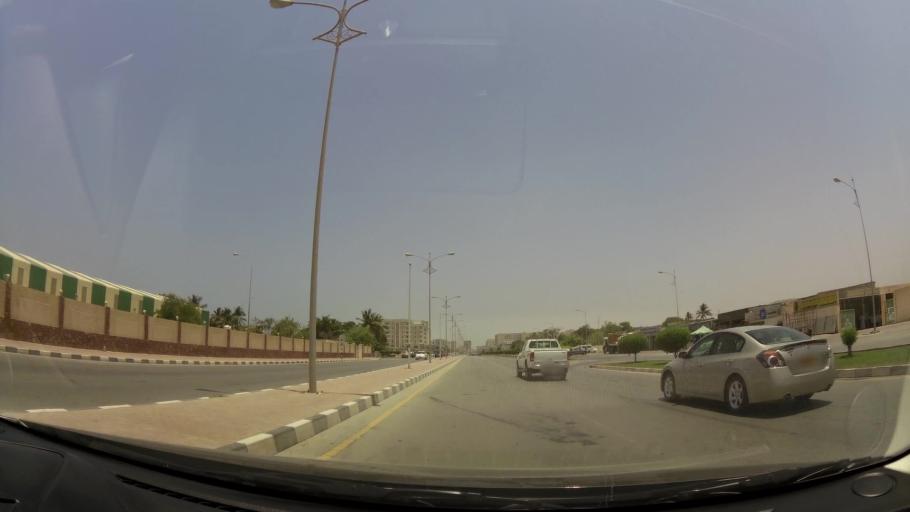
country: OM
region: Zufar
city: Salalah
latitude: 17.0208
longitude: 54.1177
